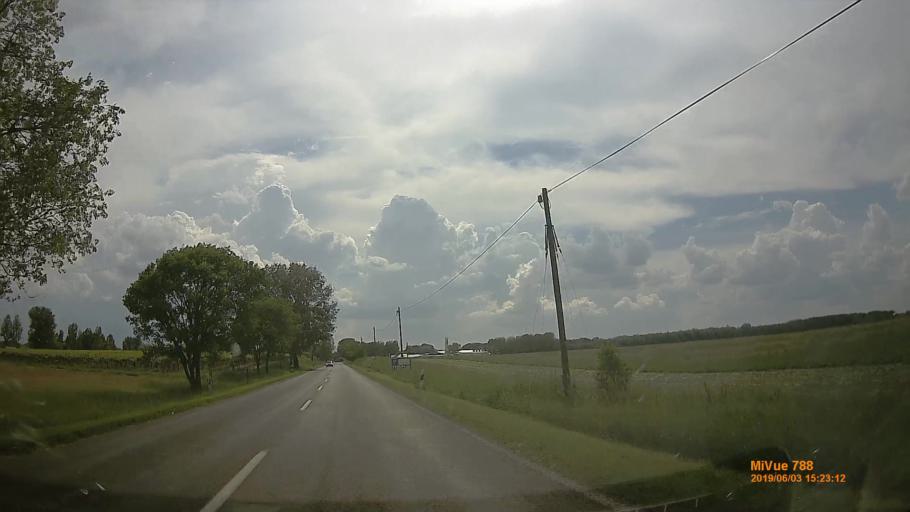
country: HU
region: Bacs-Kiskun
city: Tazlar
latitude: 46.6224
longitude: 19.4908
